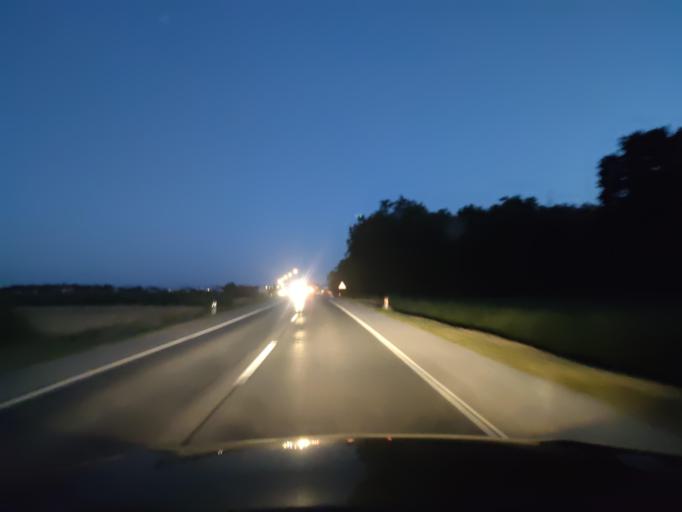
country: HR
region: Medimurska
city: Mackovec
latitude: 46.4199
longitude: 16.4259
